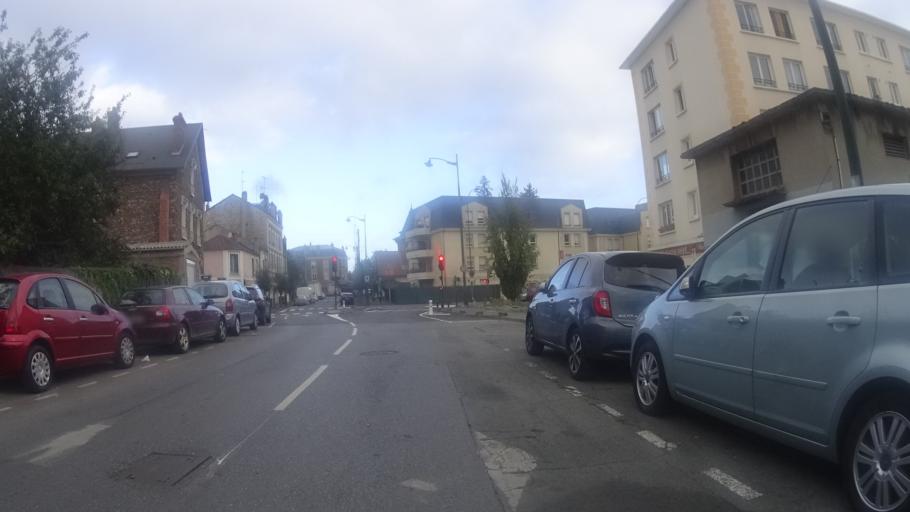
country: FR
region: Ile-de-France
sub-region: Departement de l'Essonne
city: Corbeil-Essonnes
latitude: 48.6124
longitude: 2.4760
